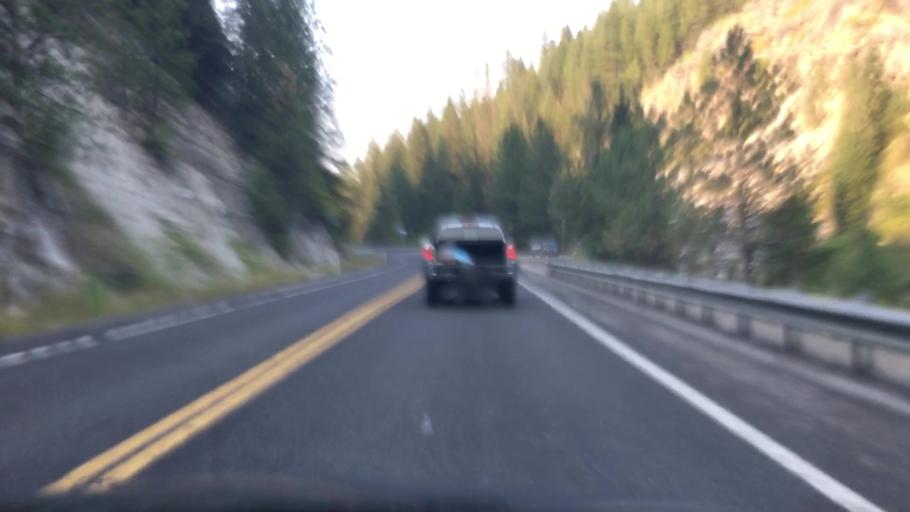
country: US
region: Idaho
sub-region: Valley County
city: Cascade
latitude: 44.2451
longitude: -116.0971
